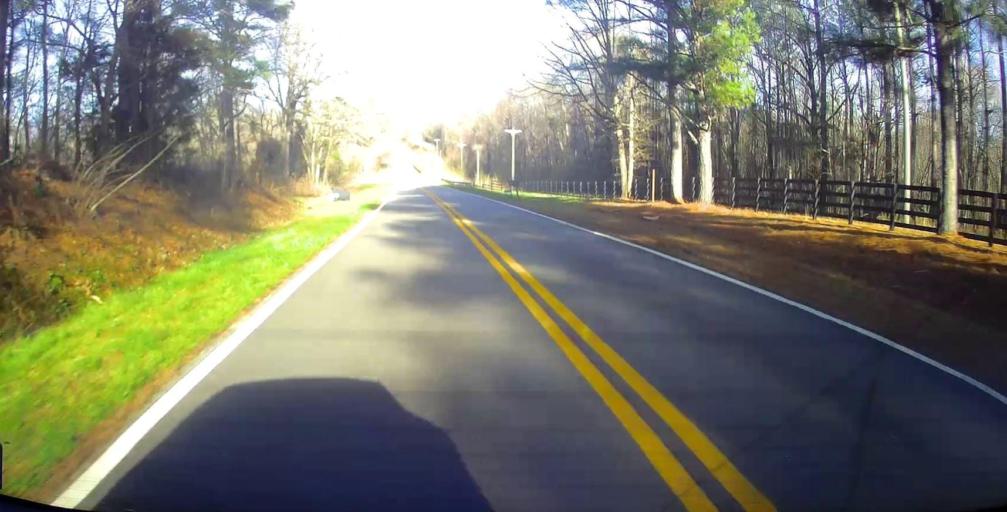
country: US
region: Georgia
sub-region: Bibb County
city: West Point
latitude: 32.8361
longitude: -83.9208
